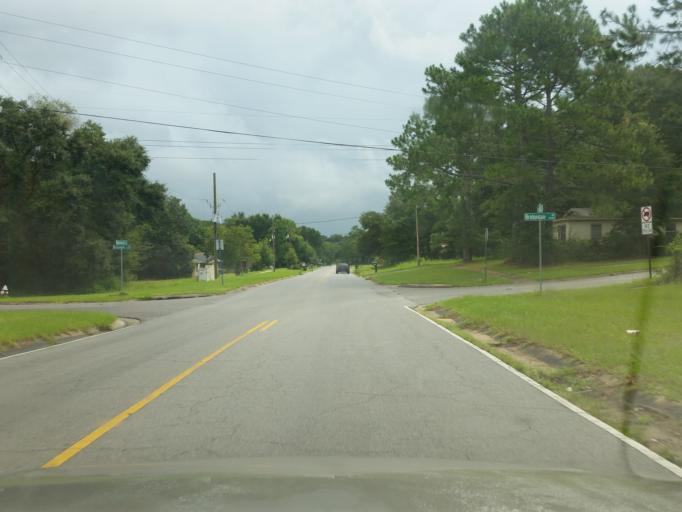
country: US
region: Florida
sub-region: Escambia County
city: West Pensacola
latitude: 30.4484
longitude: -87.2738
